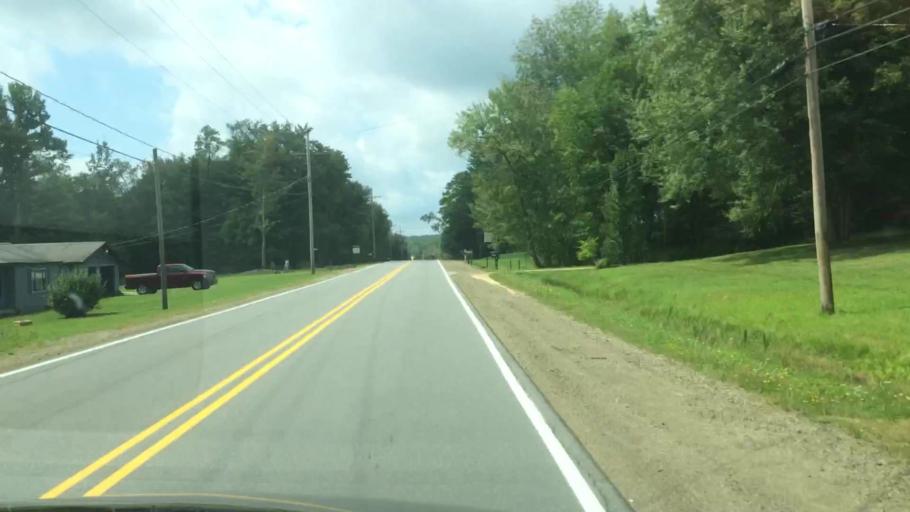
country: US
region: Pennsylvania
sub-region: McKean County
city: Bradford
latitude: 41.8766
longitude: -78.5807
